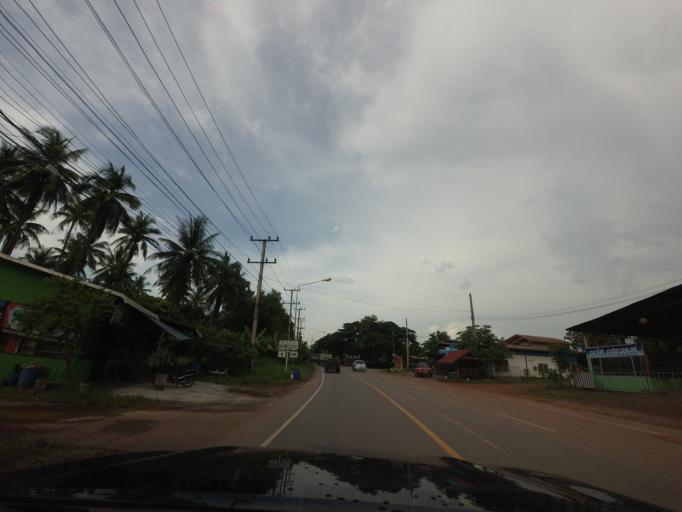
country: TH
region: Changwat Udon Thani
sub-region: Amphoe Ban Phue
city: Ban Phue
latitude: 17.6775
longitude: 102.4562
